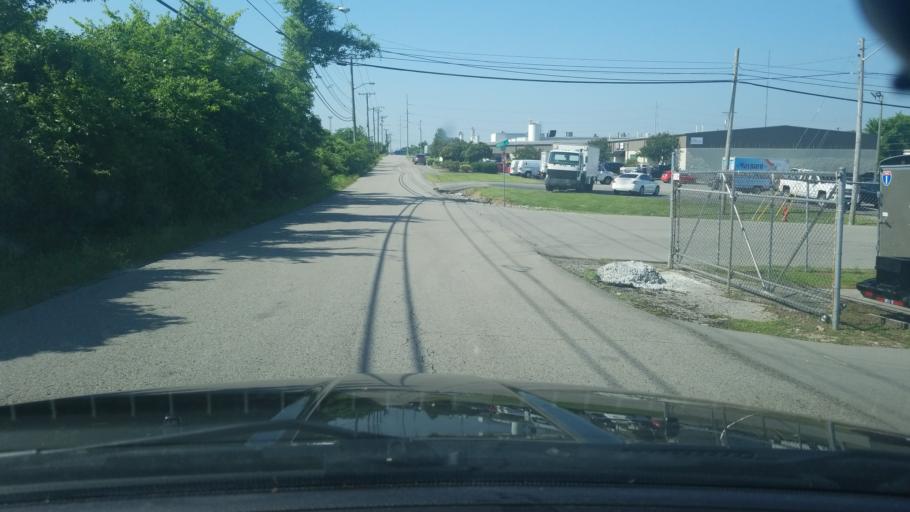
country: US
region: Tennessee
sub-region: Davidson County
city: Oak Hill
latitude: 36.1050
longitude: -86.7528
